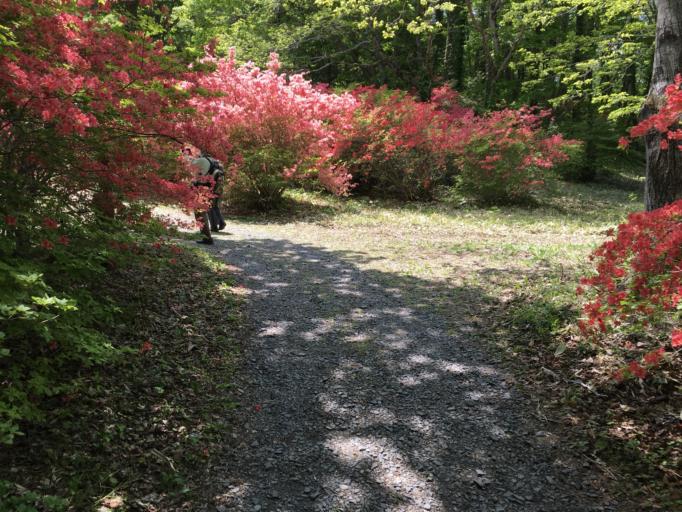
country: JP
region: Iwate
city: Ofunato
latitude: 38.8555
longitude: 141.4688
